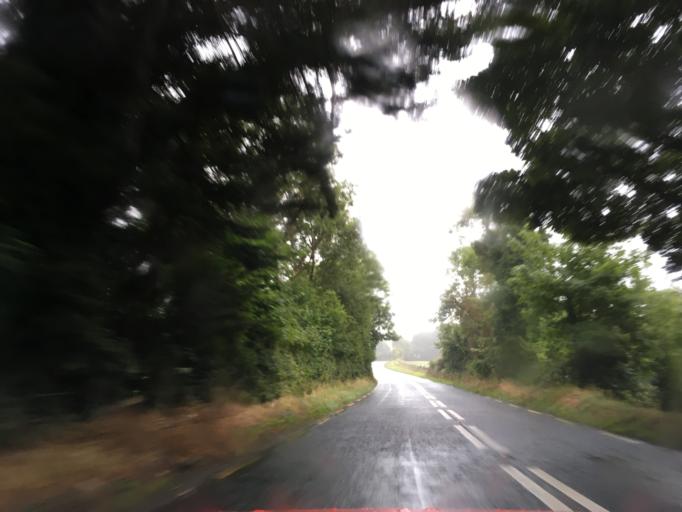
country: IE
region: Munster
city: Tipperary
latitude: 52.4786
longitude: -8.1318
